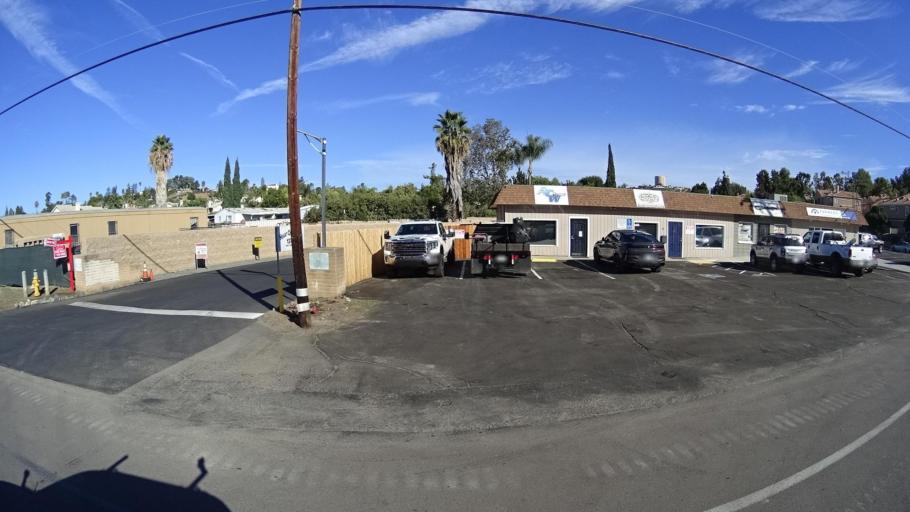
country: US
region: California
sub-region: San Diego County
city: Lakeside
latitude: 32.8416
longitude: -116.8891
